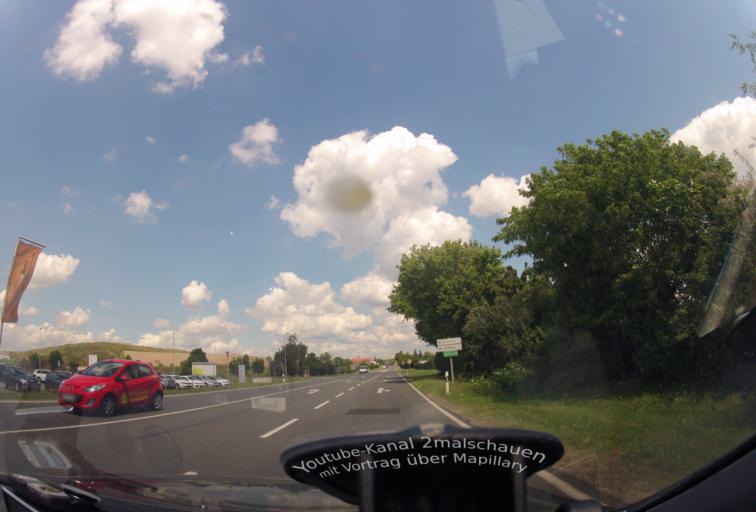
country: DE
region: Saxony
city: Zinna
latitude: 51.5570
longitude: 12.9674
